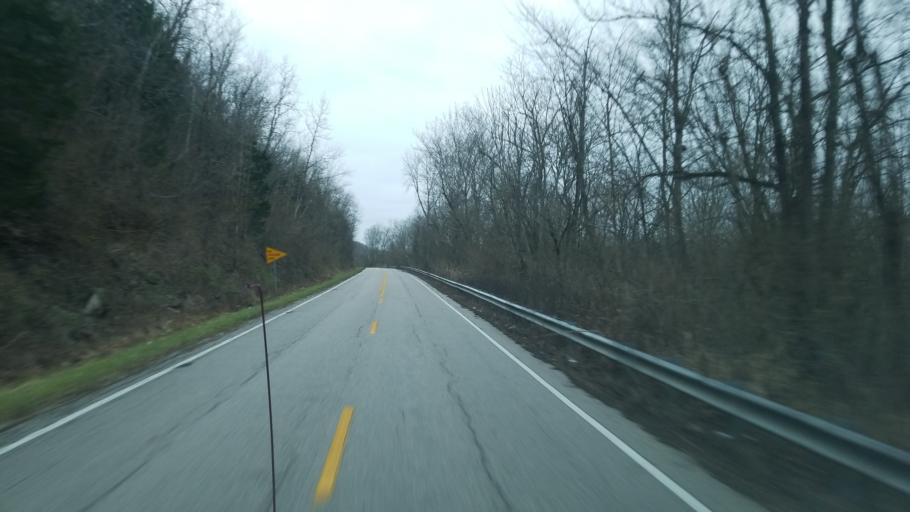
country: US
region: Kentucky
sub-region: Bracken County
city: Augusta
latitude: 38.7686
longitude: -84.0177
